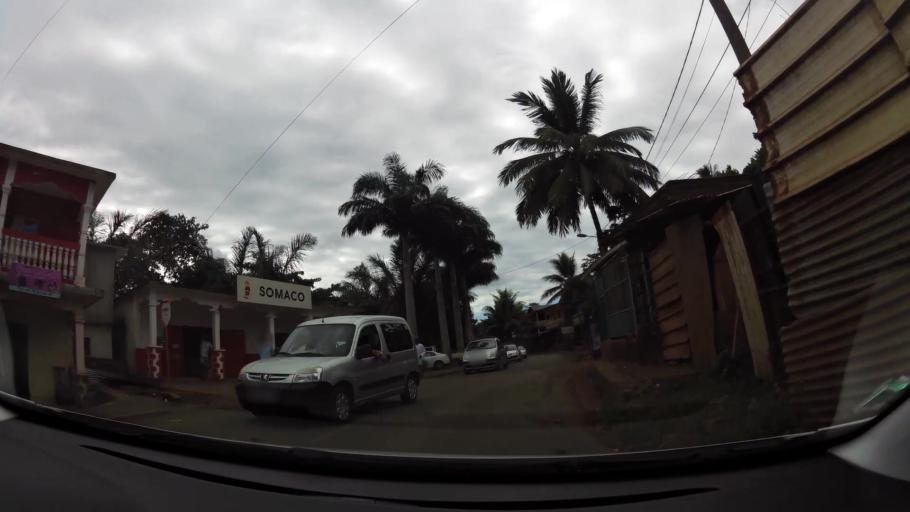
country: YT
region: Chiconi
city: Chiconi
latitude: -12.8331
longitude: 45.1147
